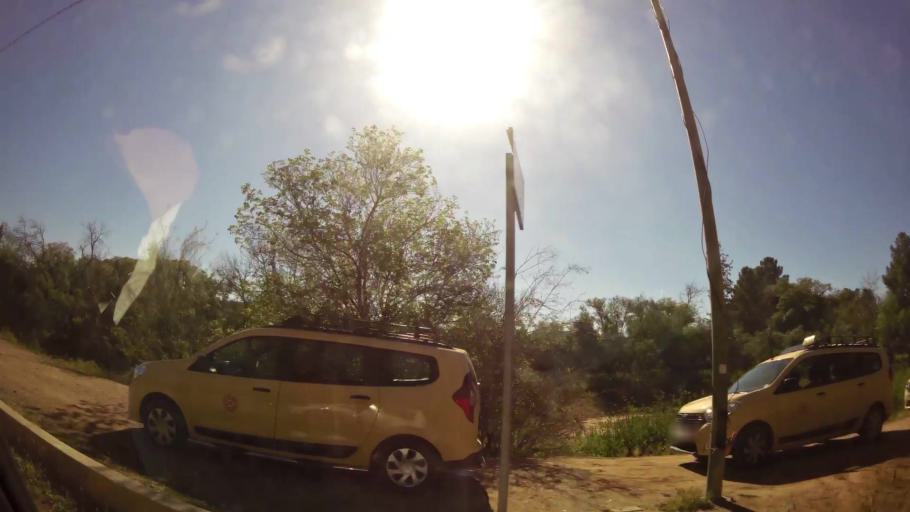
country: MA
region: Marrakech-Tensift-Al Haouz
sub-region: Marrakech
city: Marrakesh
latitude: 31.6612
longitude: -7.9349
